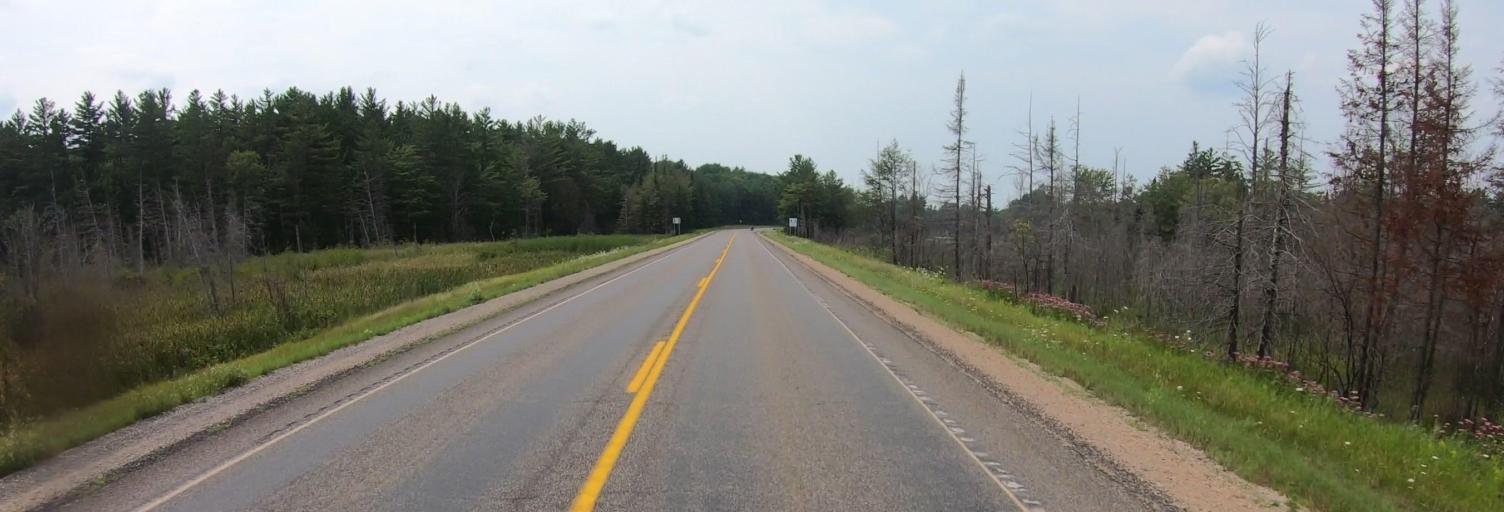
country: US
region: Michigan
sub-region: Alger County
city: Munising
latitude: 46.3329
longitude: -86.8234
